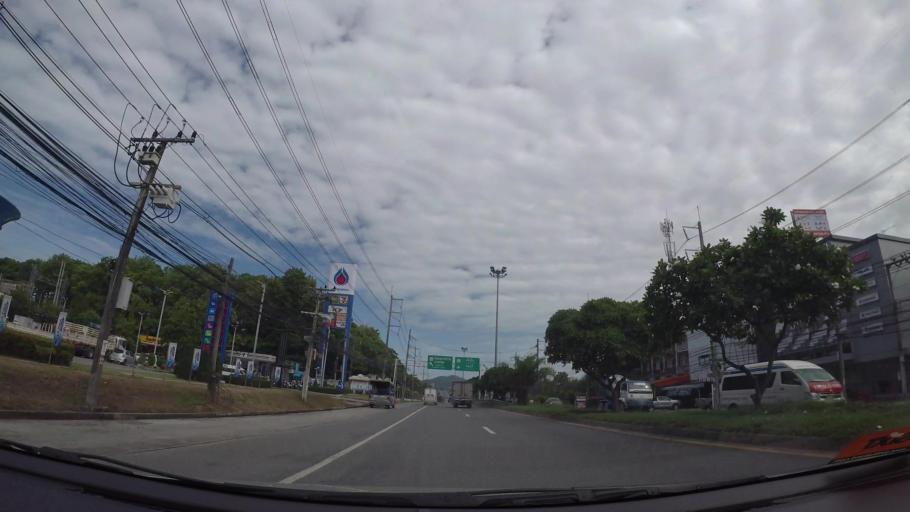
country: TH
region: Rayong
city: Ban Chang
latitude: 12.7229
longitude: 101.1520
